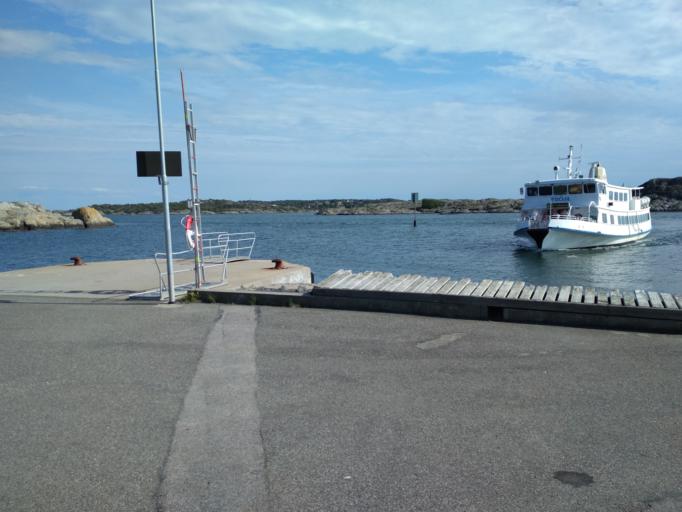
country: SE
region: Vaestra Goetaland
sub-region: Goteborg
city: Styrso
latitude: 57.6355
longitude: 11.7666
